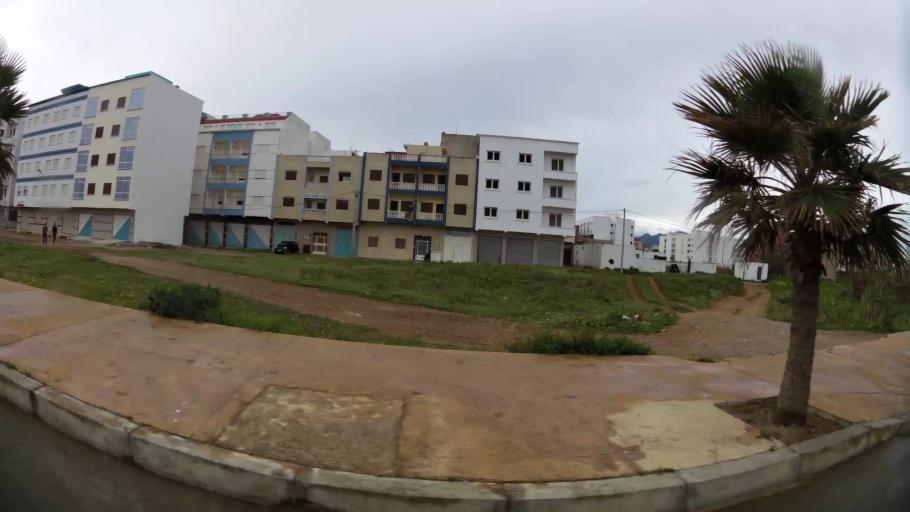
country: MA
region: Tanger-Tetouan
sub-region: Tetouan
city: Martil
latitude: 35.6308
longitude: -5.2868
